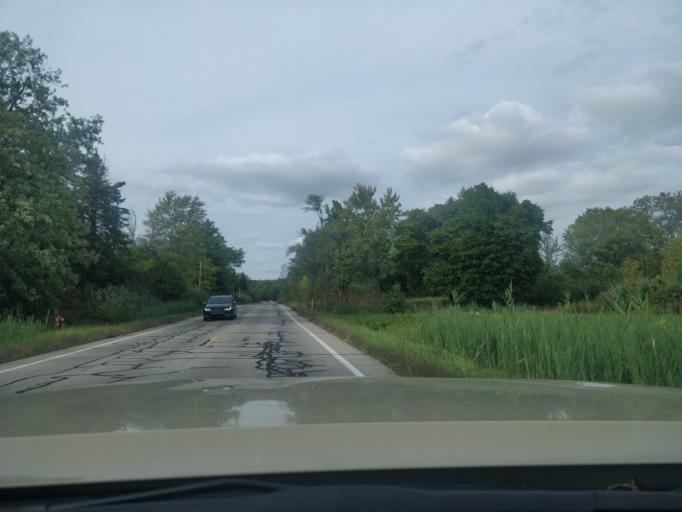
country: US
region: Michigan
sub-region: Wayne County
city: Romulus
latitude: 42.1817
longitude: -83.3706
